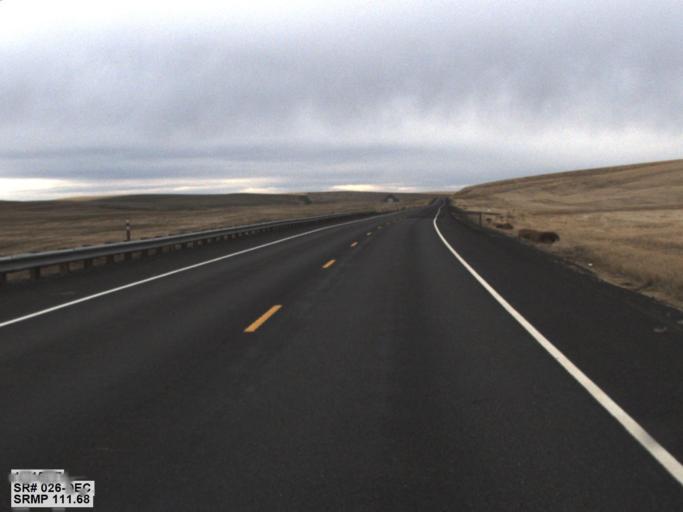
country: US
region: Washington
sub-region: Garfield County
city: Pomeroy
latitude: 46.8028
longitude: -117.7599
